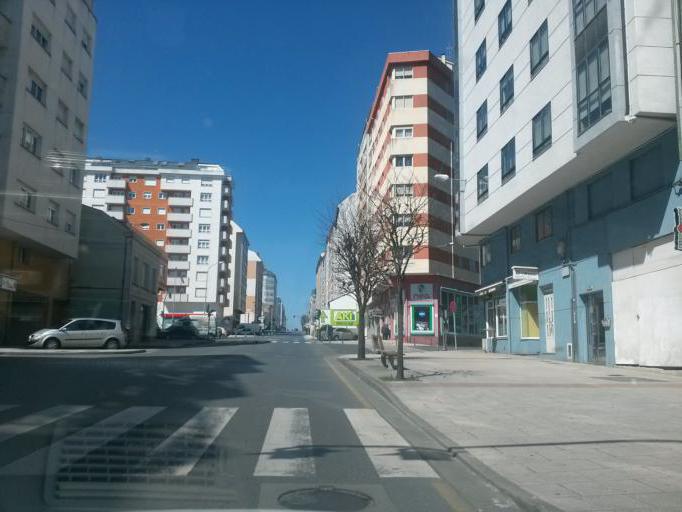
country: ES
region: Galicia
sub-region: Provincia de Lugo
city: Lugo
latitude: 43.0266
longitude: -7.5680
